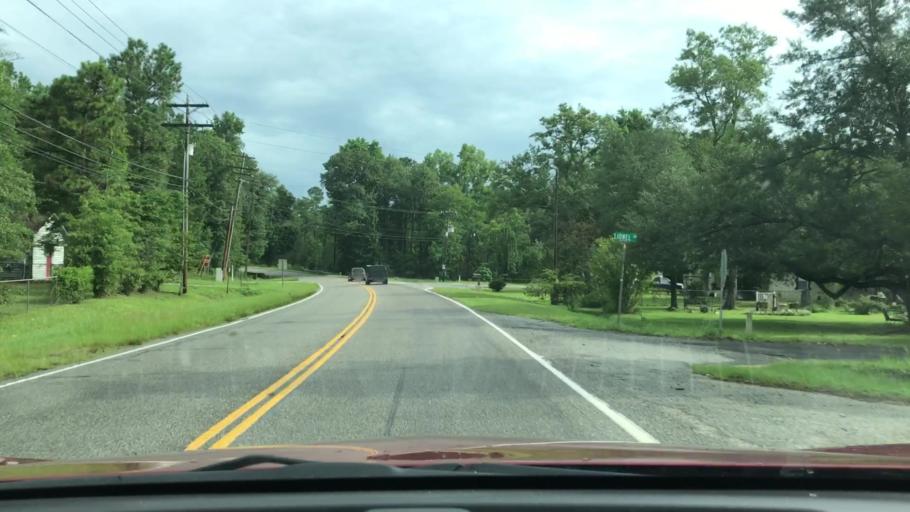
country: US
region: South Carolina
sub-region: Georgetown County
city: Georgetown
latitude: 33.4361
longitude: -79.2765
